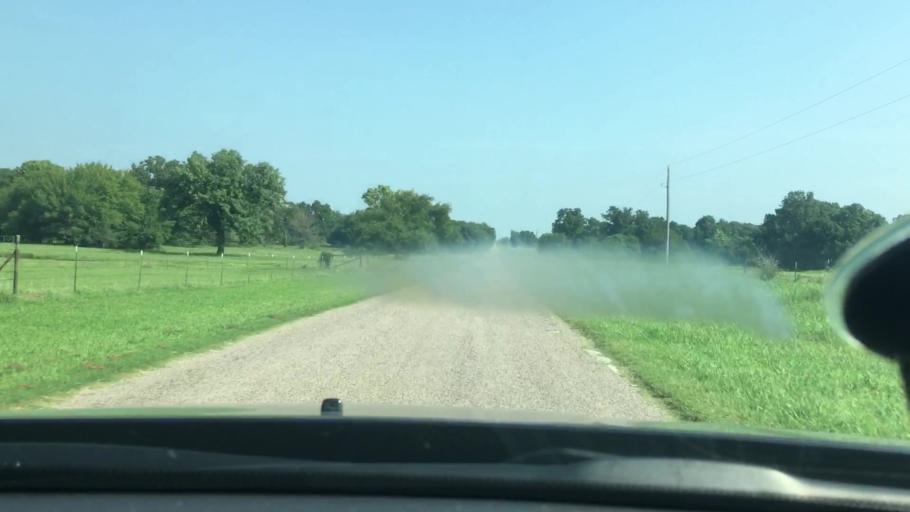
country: US
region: Oklahoma
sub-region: Pontotoc County
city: Ada
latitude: 34.6696
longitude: -96.5298
